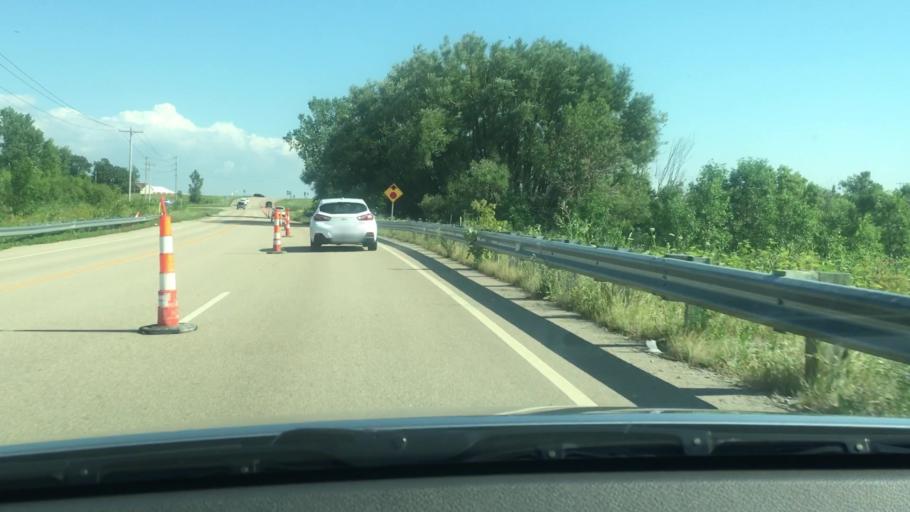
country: US
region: Wisconsin
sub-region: Winnebago County
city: Oshkosh
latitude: 43.9553
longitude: -88.5821
